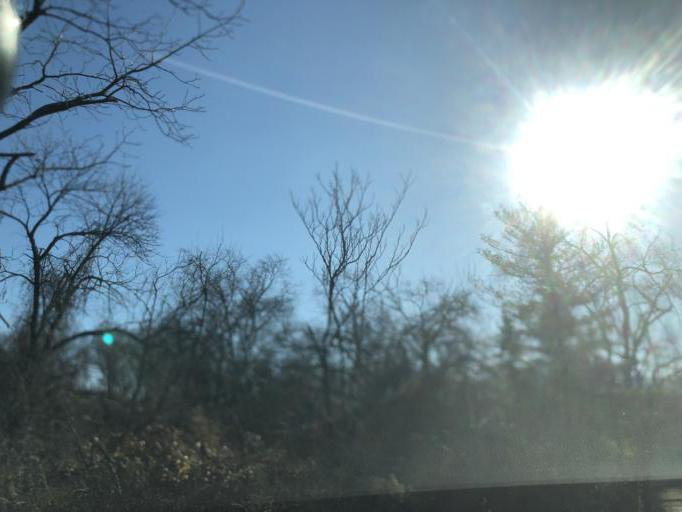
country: US
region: Pennsylvania
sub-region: Delaware County
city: Millbourne
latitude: 39.9567
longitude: -75.2501
